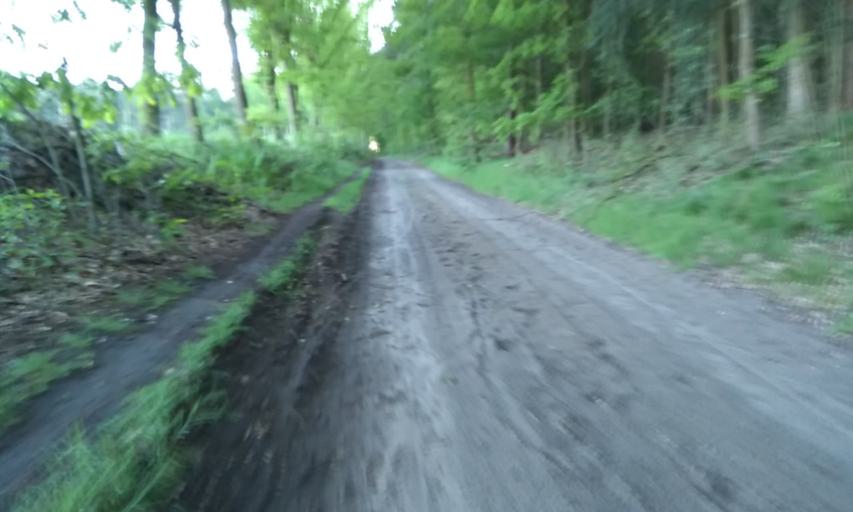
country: DE
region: Lower Saxony
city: Bliedersdorf
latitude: 53.4924
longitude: 9.5446
